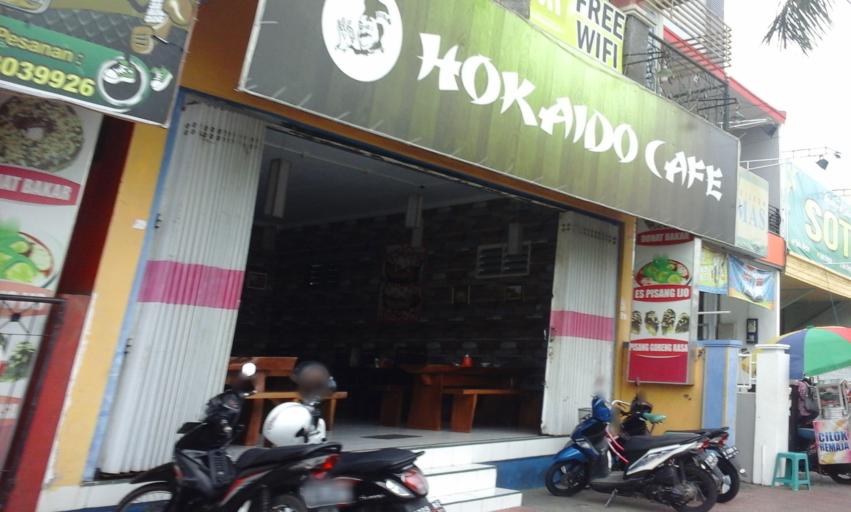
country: ID
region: East Java
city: Krajan
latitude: -8.2180
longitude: 114.3693
